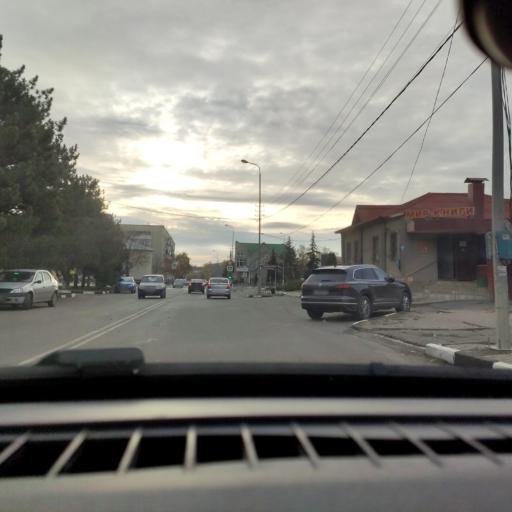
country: RU
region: Belgorod
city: Alekseyevka
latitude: 50.6285
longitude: 38.6878
